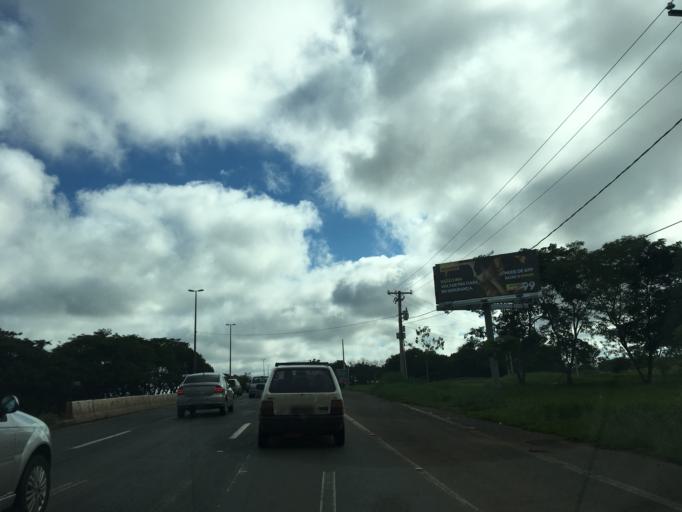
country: BR
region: Federal District
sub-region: Brasilia
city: Brasilia
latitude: -15.8671
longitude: -47.9442
